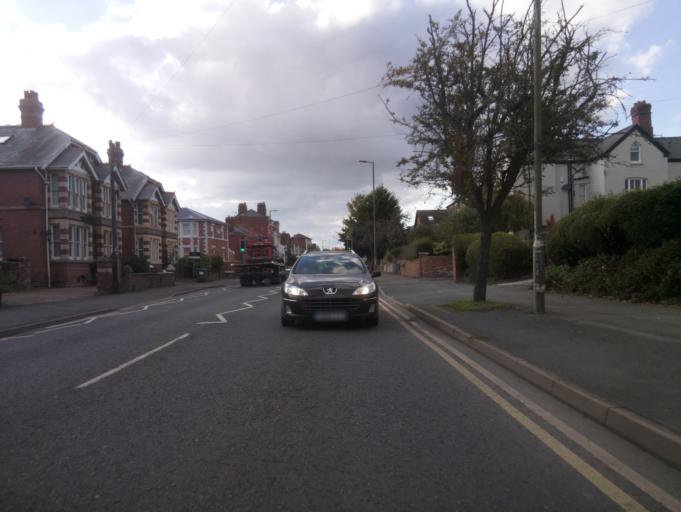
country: GB
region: England
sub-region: Herefordshire
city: Belmont
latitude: 52.0598
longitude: -2.7339
